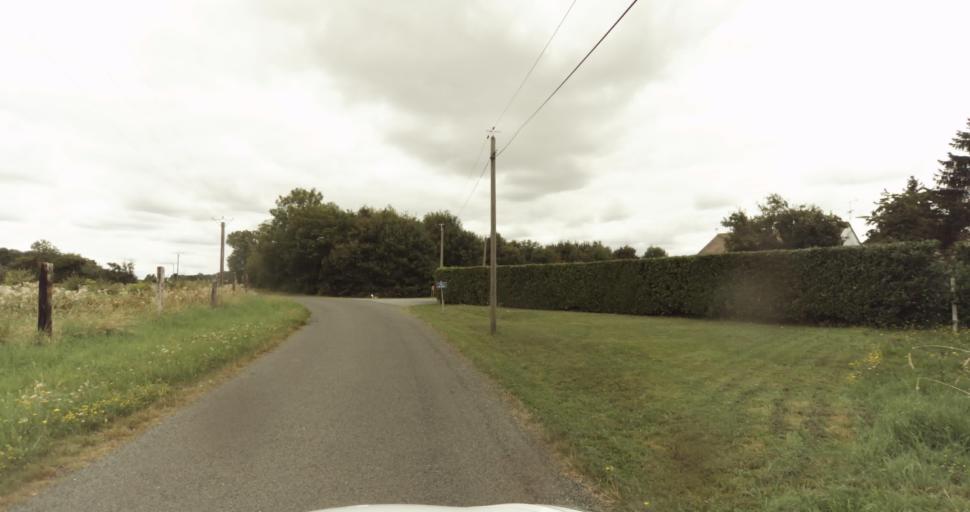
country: FR
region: Haute-Normandie
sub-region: Departement de l'Eure
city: La Madeleine-de-Nonancourt
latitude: 48.8331
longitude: 1.2235
